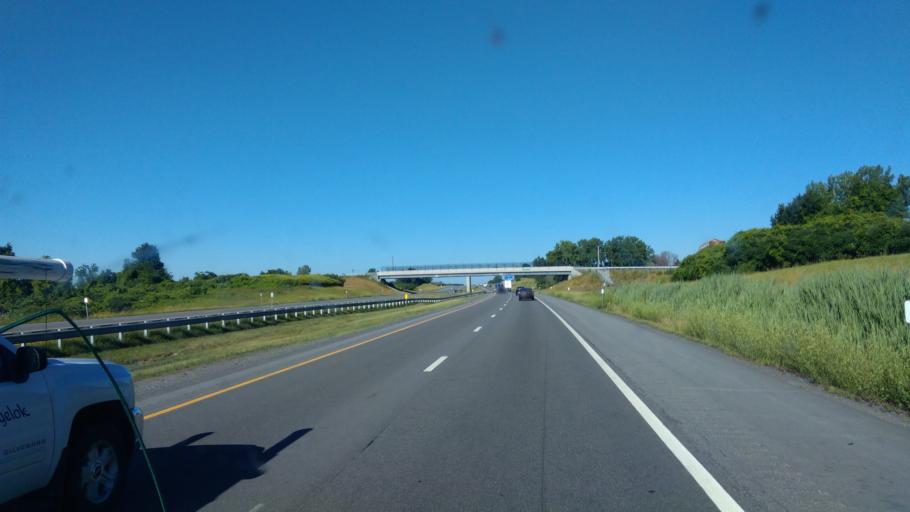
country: US
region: New York
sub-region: Monroe County
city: Scottsville
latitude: 43.0426
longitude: -77.7936
